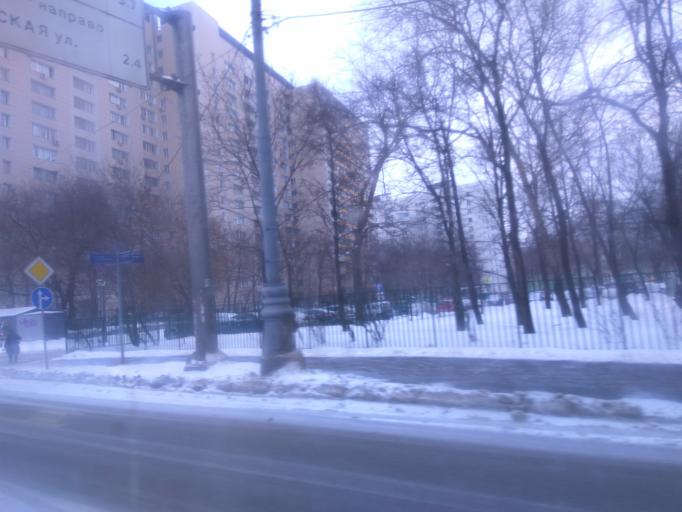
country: RU
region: Moscow
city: Mar'ina Roshcha
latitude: 55.7915
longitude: 37.6373
